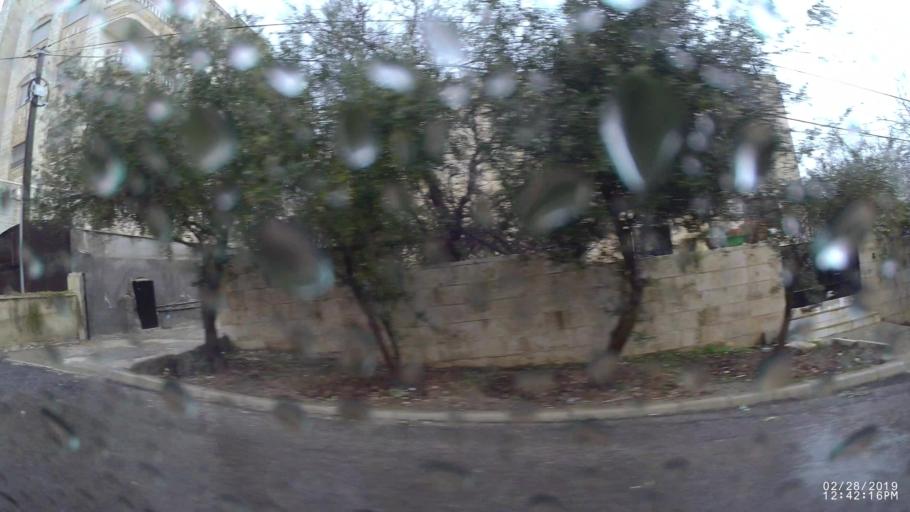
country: JO
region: Amman
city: Al Jubayhah
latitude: 32.0292
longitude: 35.8859
